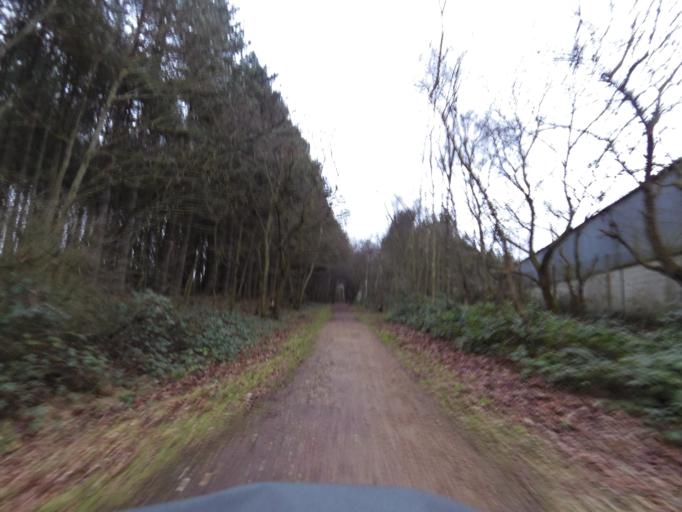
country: GB
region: England
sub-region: Norfolk
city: Costessey
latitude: 52.7163
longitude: 1.1361
